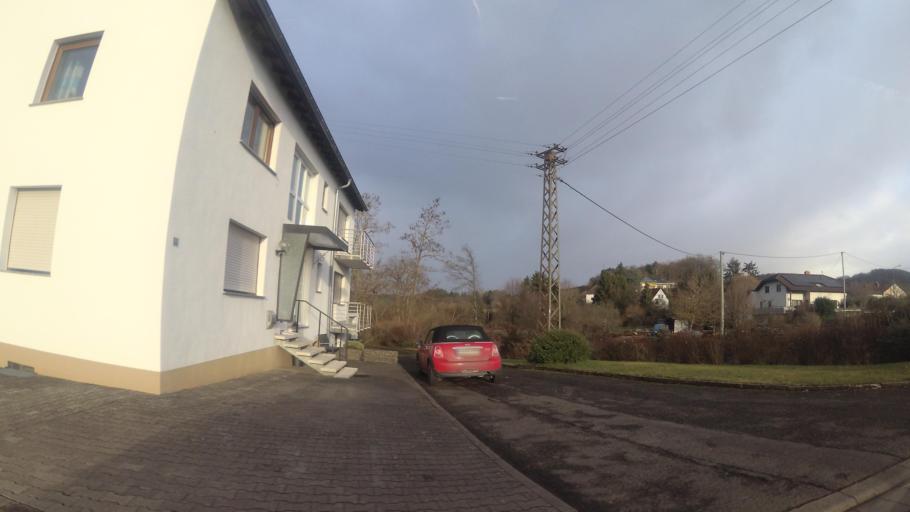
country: DE
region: Rheinland-Pfalz
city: Ulmet
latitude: 49.5899
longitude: 7.4529
